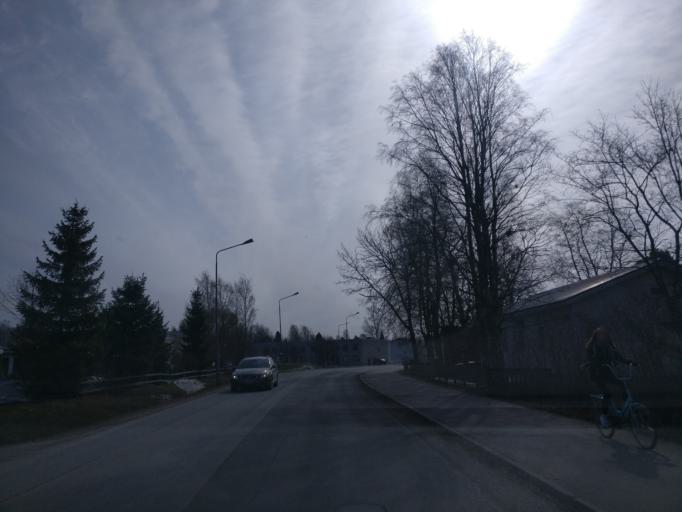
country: FI
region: Lapland
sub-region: Kemi-Tornio
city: Kemi
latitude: 65.7505
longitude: 24.5593
